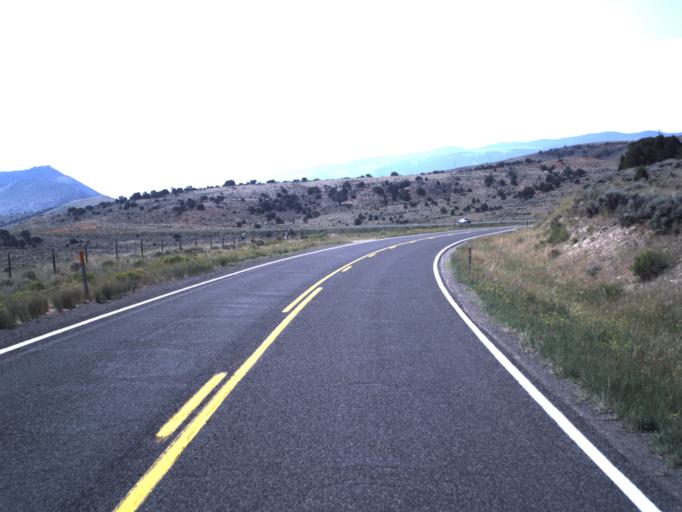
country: US
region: Utah
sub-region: Daggett County
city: Manila
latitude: 40.9861
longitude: -109.8425
